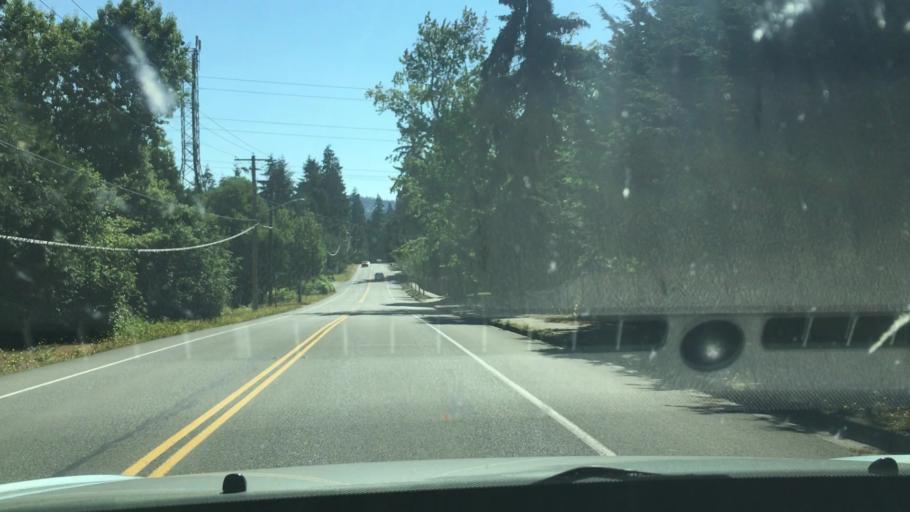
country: US
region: Washington
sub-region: King County
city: Newcastle
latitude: 47.5410
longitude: -122.1768
